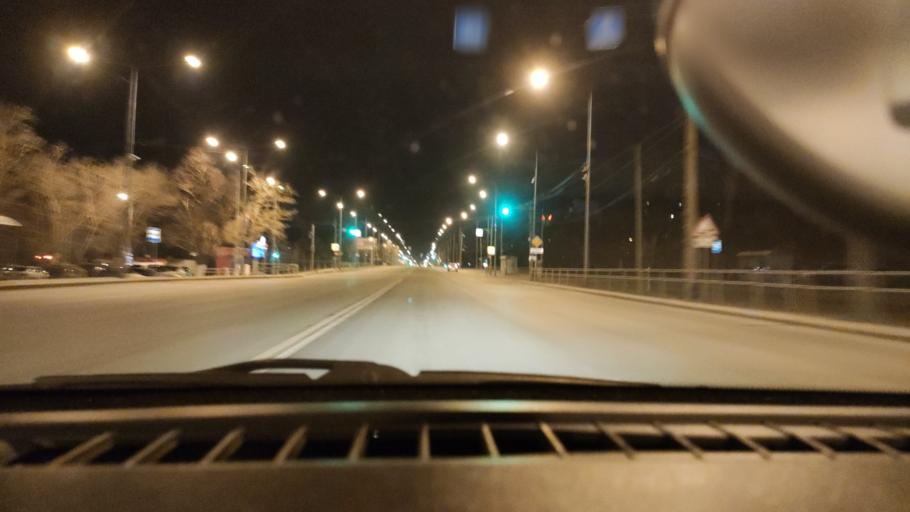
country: RU
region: Samara
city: Samara
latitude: 53.2404
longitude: 50.1983
